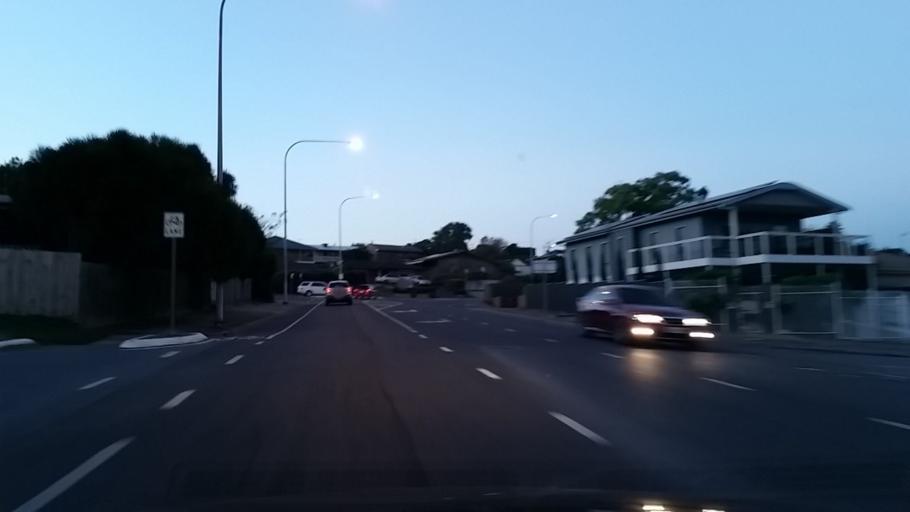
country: AU
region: South Australia
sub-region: Adelaide
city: Port Noarlunga
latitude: -35.1473
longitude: 138.4760
